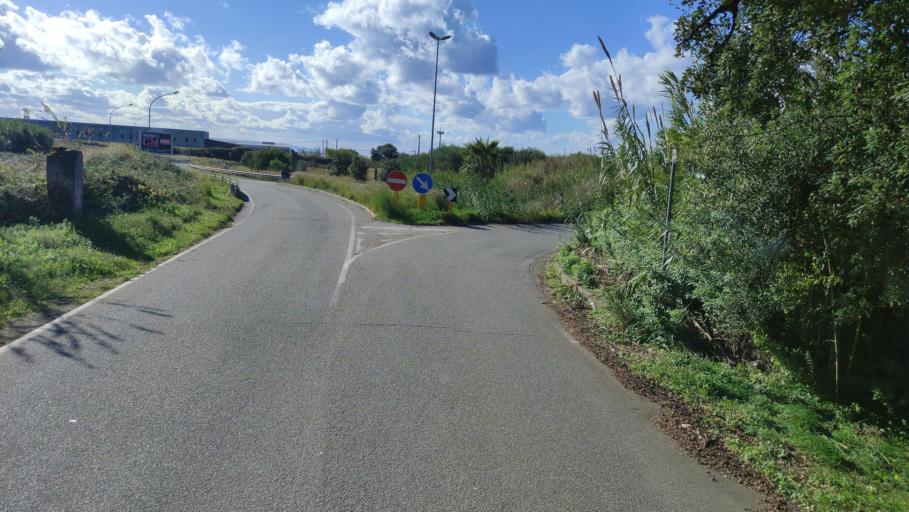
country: IT
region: Calabria
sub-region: Provincia di Catanzaro
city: Santa Eufemia Lamezia
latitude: 38.9204
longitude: 16.2750
